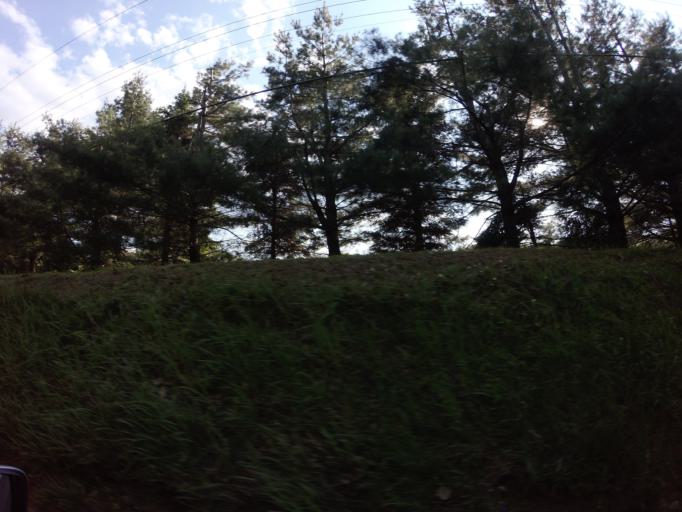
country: US
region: Maryland
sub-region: Baltimore County
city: Mays Chapel
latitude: 39.4512
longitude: -76.6870
